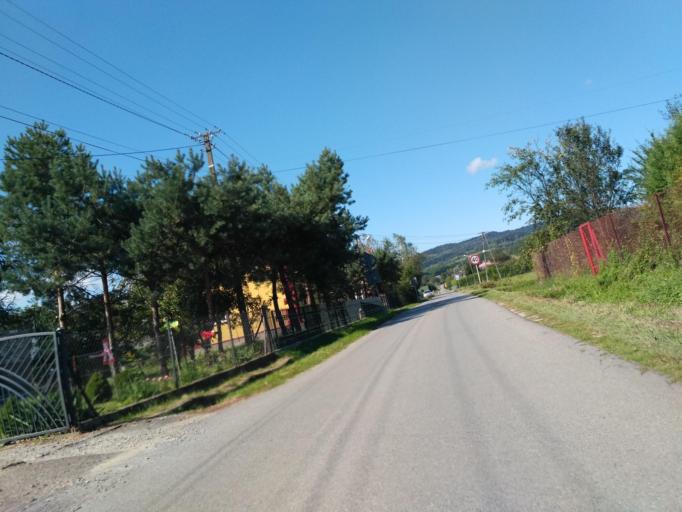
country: PL
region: Subcarpathian Voivodeship
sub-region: Powiat jasielski
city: Kolaczyce
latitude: 49.8043
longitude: 21.4162
